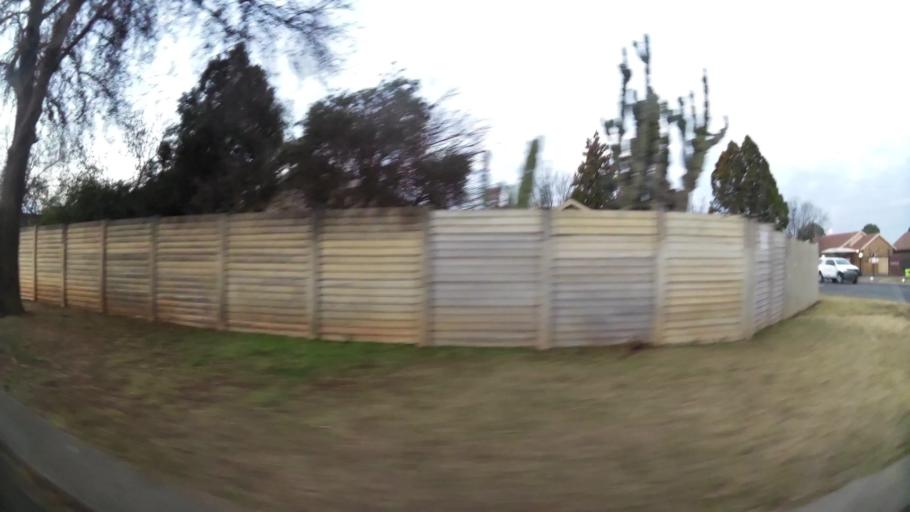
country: ZA
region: Orange Free State
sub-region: Mangaung Metropolitan Municipality
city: Bloemfontein
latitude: -29.1667
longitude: 26.1978
